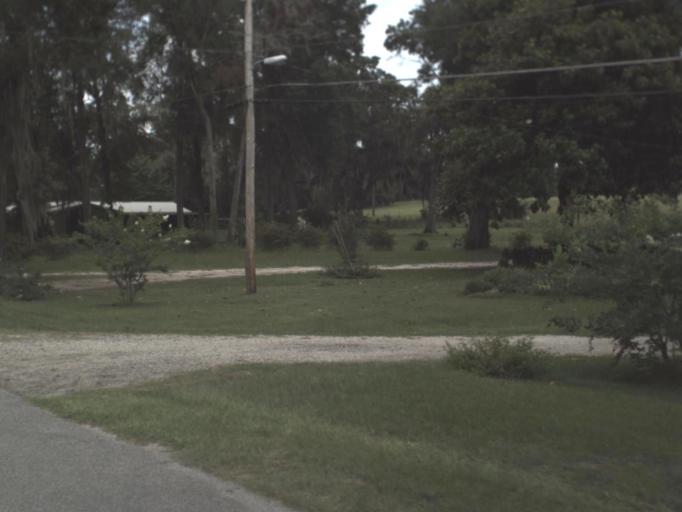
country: US
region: Florida
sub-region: Madison County
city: Madison
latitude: 30.4909
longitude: -83.4204
